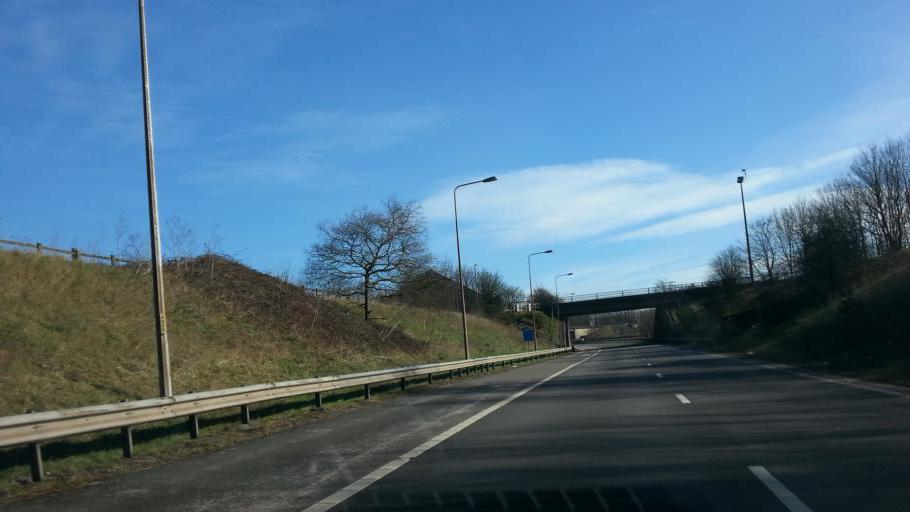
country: GB
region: England
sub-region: Solihull
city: Chelmsley Wood
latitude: 52.4797
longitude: -1.7155
